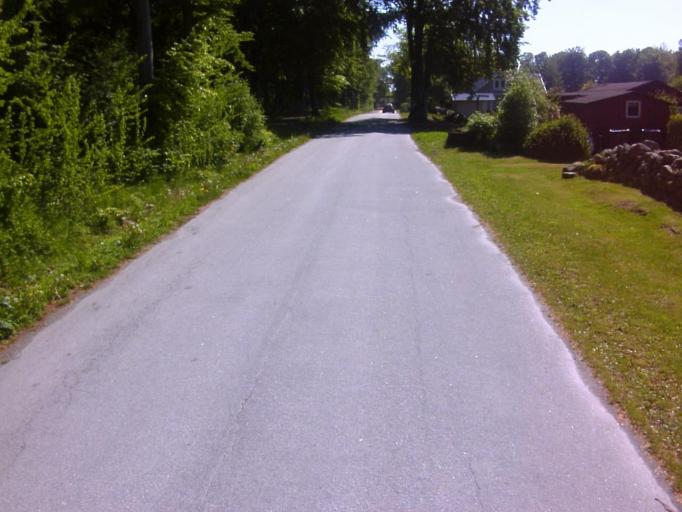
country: SE
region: Blekinge
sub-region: Solvesborgs Kommun
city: Soelvesborg
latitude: 56.0308
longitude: 14.5641
